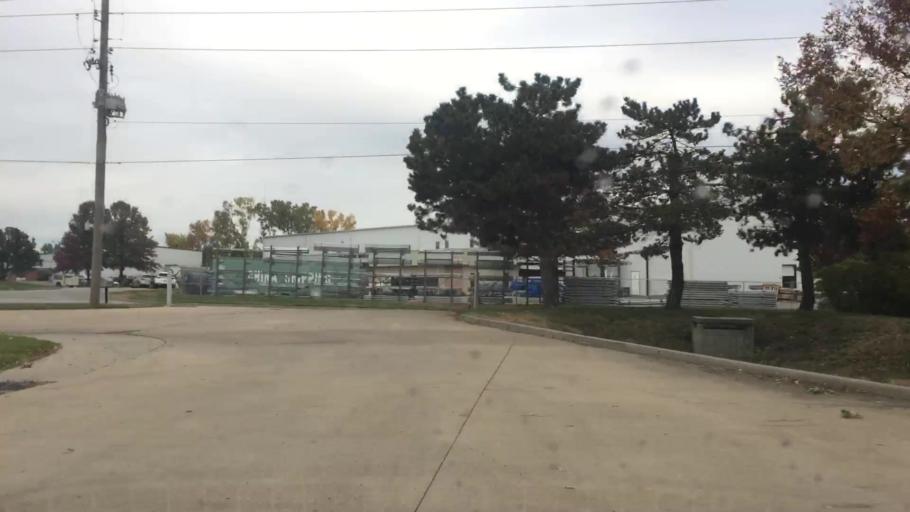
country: US
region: Missouri
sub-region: Jackson County
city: Lees Summit
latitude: 38.8953
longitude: -94.3616
